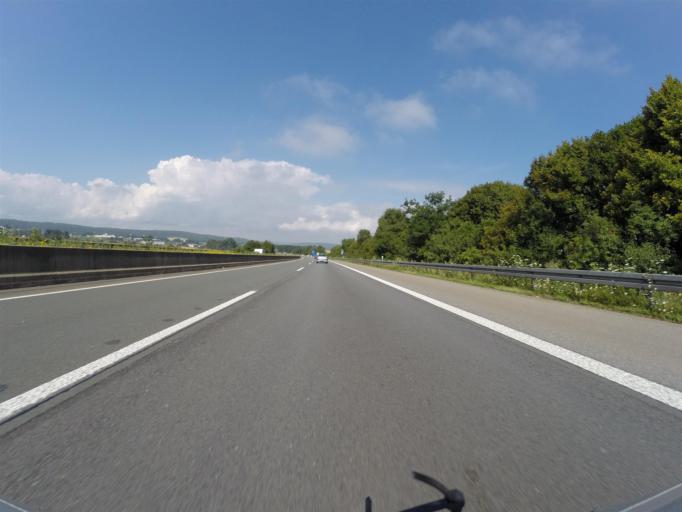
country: DE
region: Hesse
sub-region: Regierungsbezirk Kassel
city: Bad Arolsen
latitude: 51.4879
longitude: 9.0256
